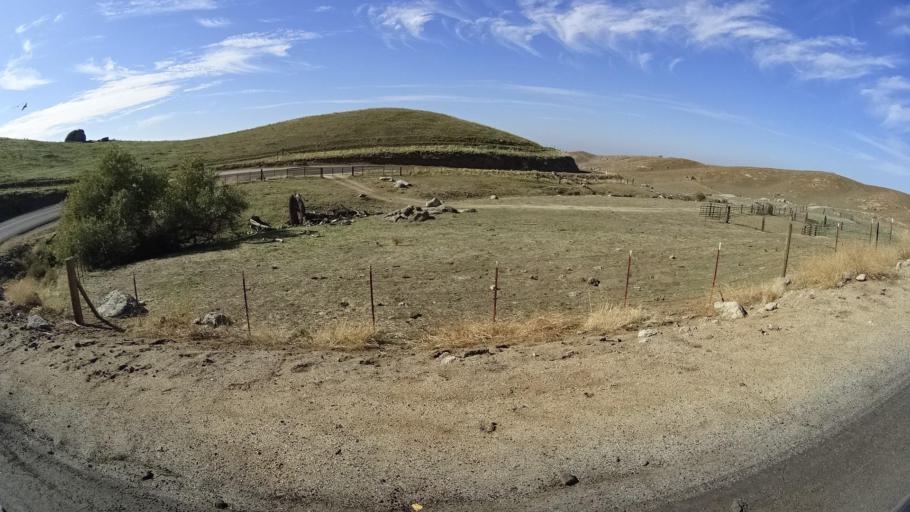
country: US
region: California
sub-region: Tulare County
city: Richgrove
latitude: 35.6830
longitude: -118.8885
